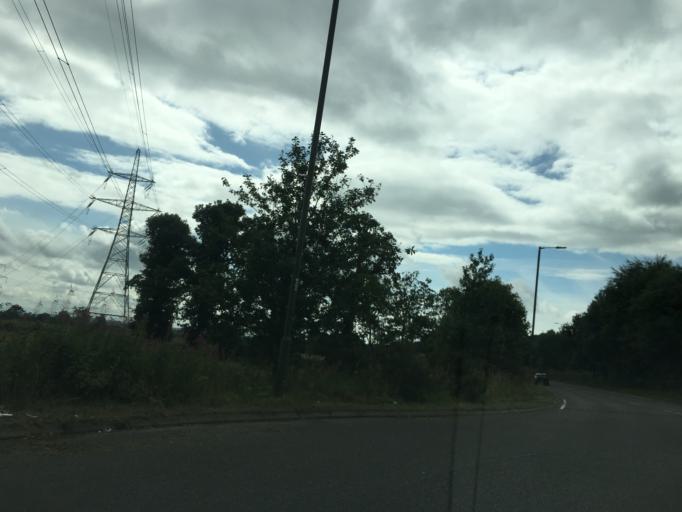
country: GB
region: Scotland
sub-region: Stirling
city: Stirling
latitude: 56.1471
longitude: -3.9022
